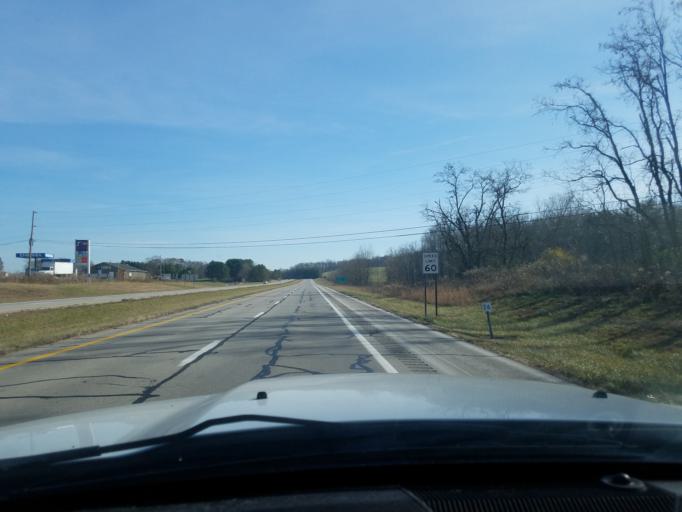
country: US
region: Ohio
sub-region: Pike County
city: Piketon
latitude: 39.0155
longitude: -82.8456
